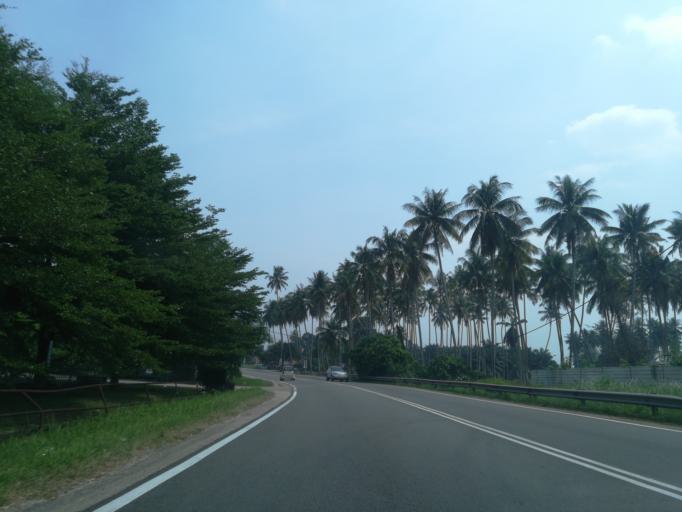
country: MY
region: Penang
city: Tasek Glugor
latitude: 5.4272
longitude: 100.5364
